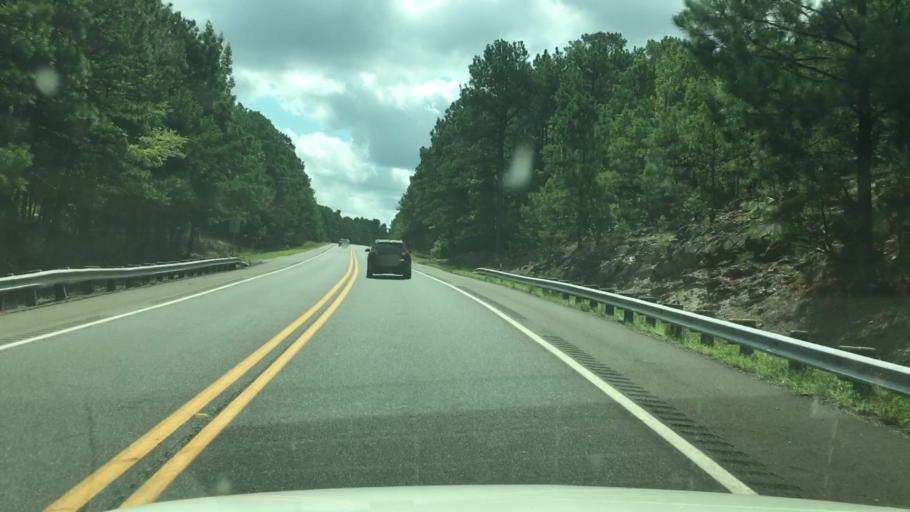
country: US
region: Arkansas
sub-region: Clark County
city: Arkadelphia
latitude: 34.2306
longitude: -93.0969
